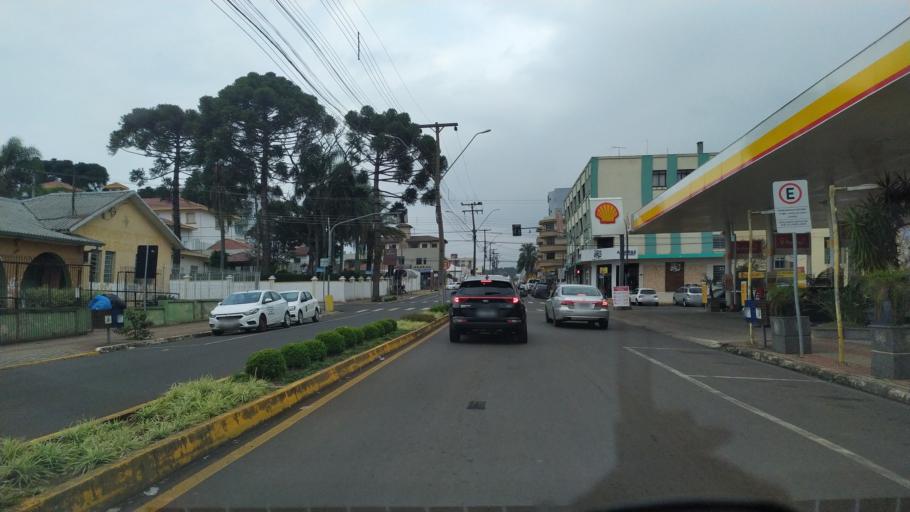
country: BR
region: Parana
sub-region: Palmas
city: Palmas
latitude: -26.4851
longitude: -51.9911
